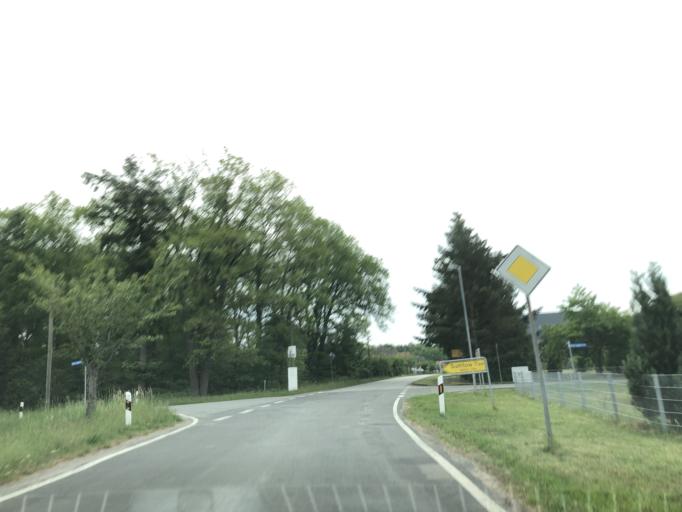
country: DE
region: Brandenburg
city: Plattenburg
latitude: 52.9433
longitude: 12.0998
